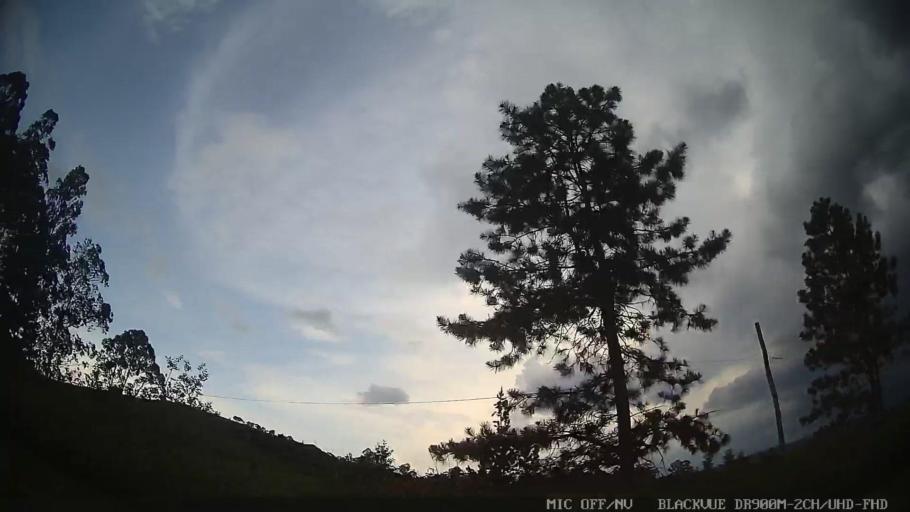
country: BR
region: Sao Paulo
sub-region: Itatiba
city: Itatiba
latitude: -22.9512
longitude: -46.8188
